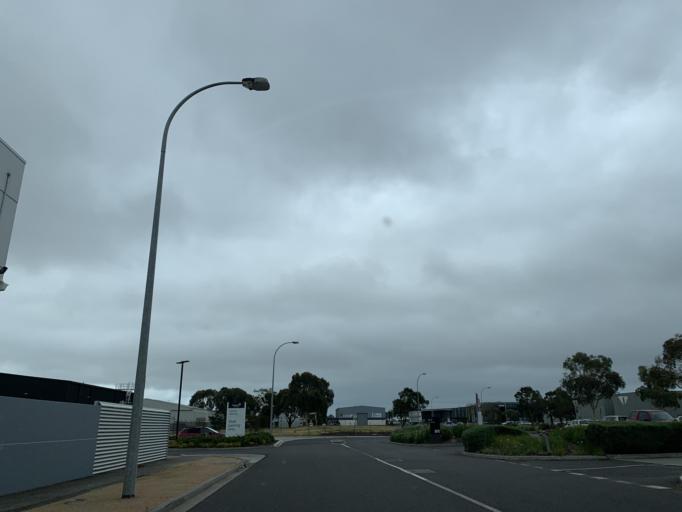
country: AU
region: Victoria
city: Heatherton
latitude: -37.9708
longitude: 145.0906
